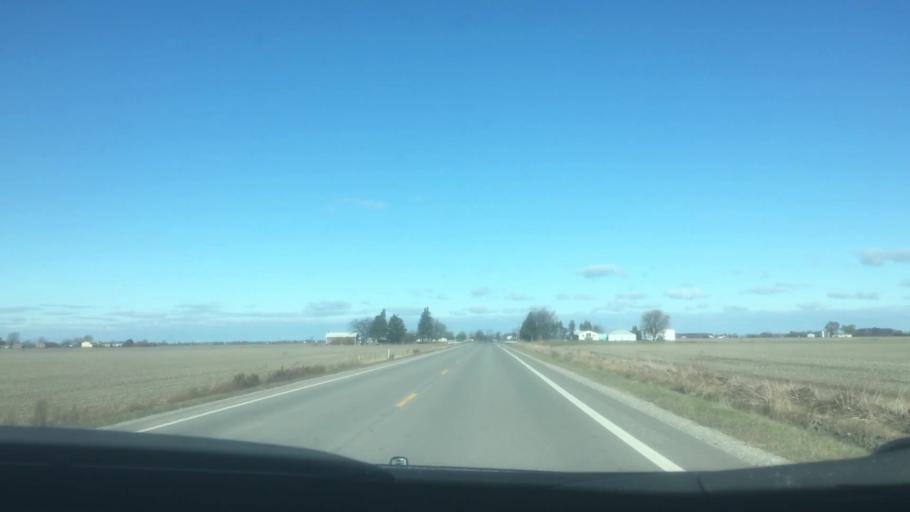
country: US
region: Michigan
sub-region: Tuscola County
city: Reese
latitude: 43.5266
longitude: -83.7586
